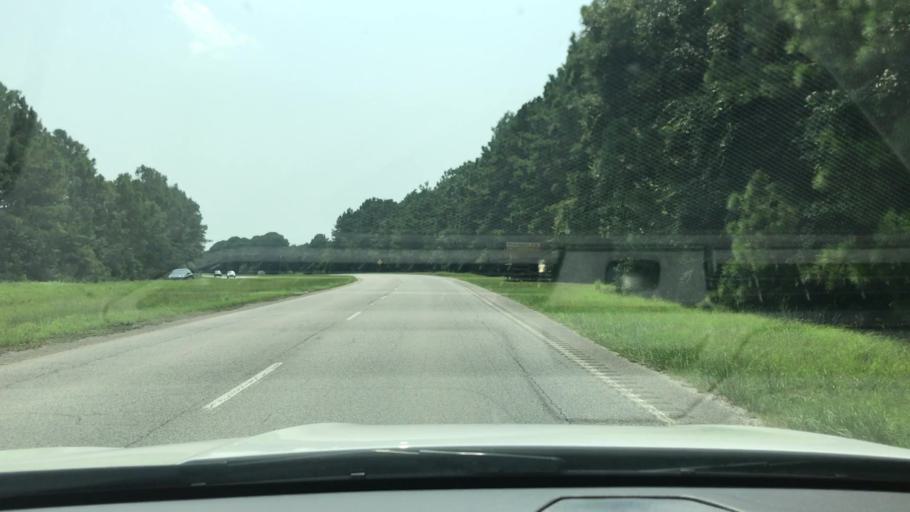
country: US
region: South Carolina
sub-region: Charleston County
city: Awendaw
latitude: 32.9454
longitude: -79.7034
